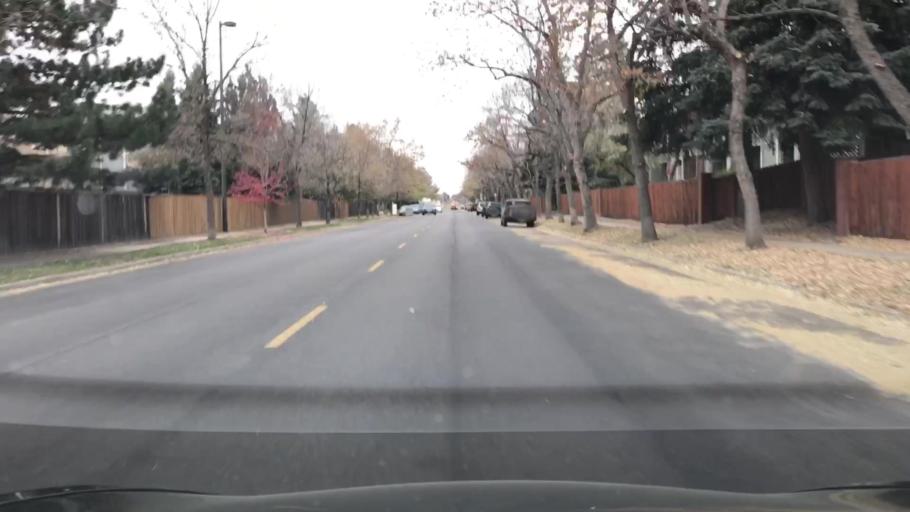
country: US
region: Colorado
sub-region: Arapahoe County
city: Glendale
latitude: 39.6894
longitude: -104.8994
